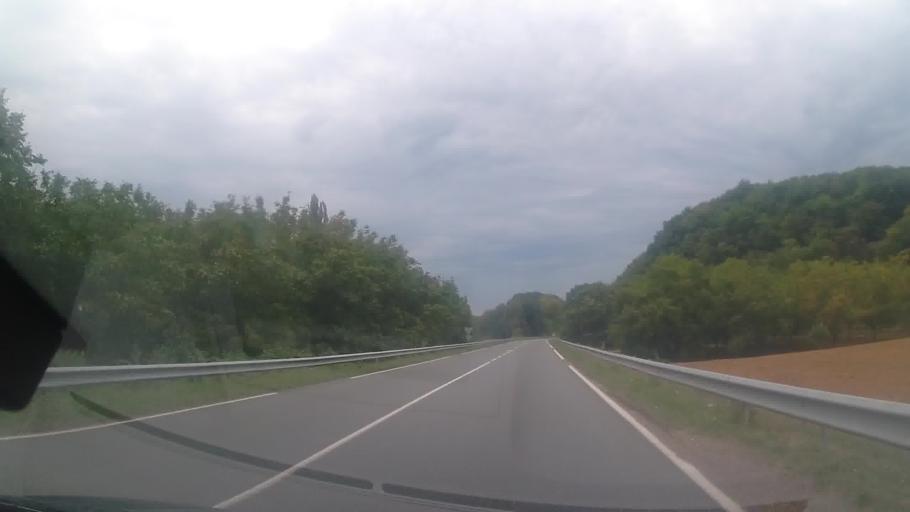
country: FR
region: Aquitaine
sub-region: Departement de la Dordogne
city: Carsac-Aillac
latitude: 44.8475
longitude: 1.3112
